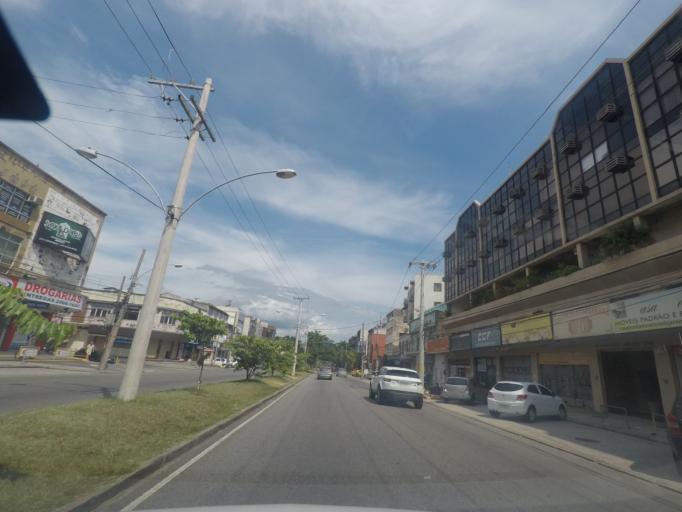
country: BR
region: Rio de Janeiro
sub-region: Rio De Janeiro
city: Rio de Janeiro
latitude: -22.8108
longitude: -43.1944
